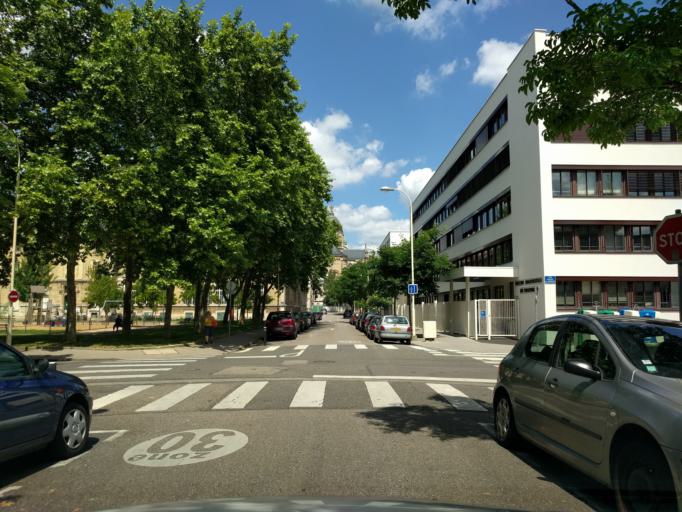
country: FR
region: Lorraine
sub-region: Departement de Meurthe-et-Moselle
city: Laxou
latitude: 48.6833
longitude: 6.1633
